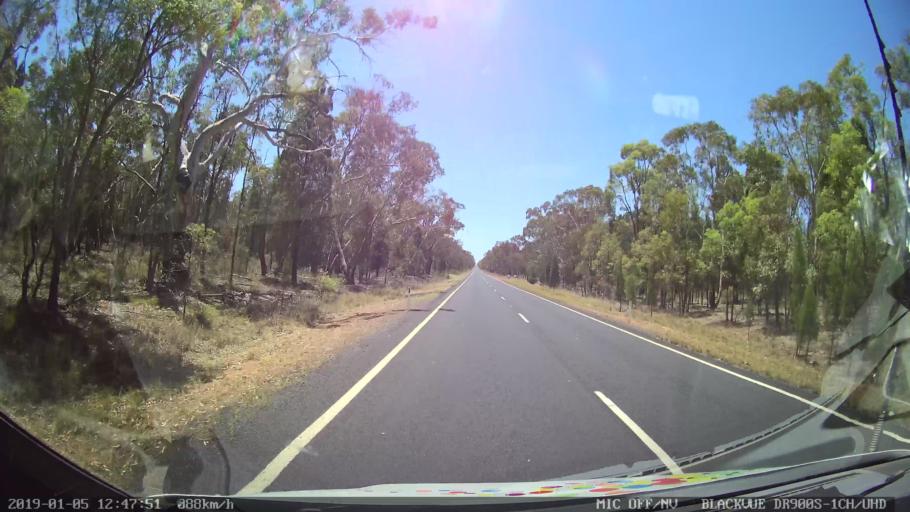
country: AU
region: New South Wales
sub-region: Warrumbungle Shire
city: Coonabarabran
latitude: -31.1182
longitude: 149.5827
